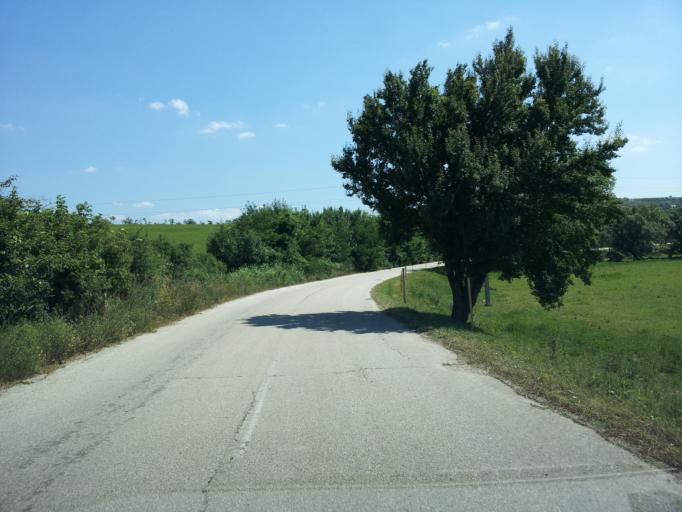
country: HU
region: Fejer
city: Many
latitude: 47.5305
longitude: 18.5843
